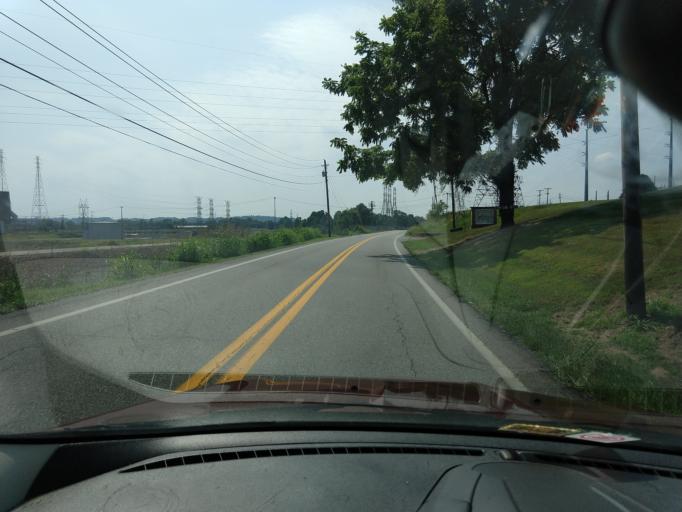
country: US
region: West Virginia
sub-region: Mason County
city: New Haven
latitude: 38.9683
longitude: -81.9300
